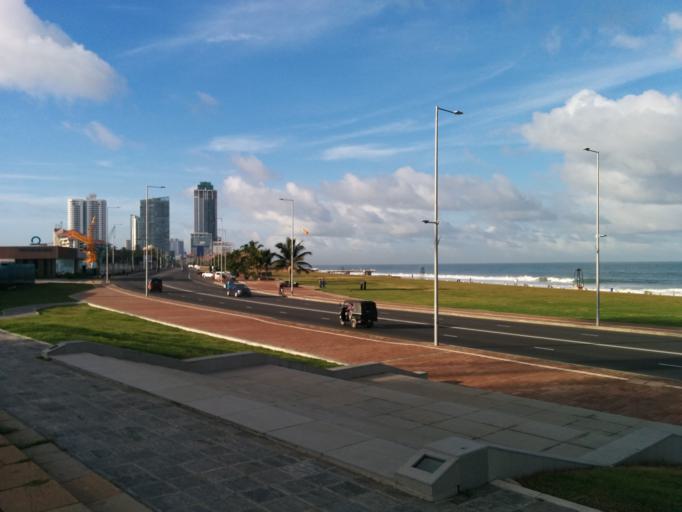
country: LK
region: Western
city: Colombo
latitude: 6.9282
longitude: 79.8438
